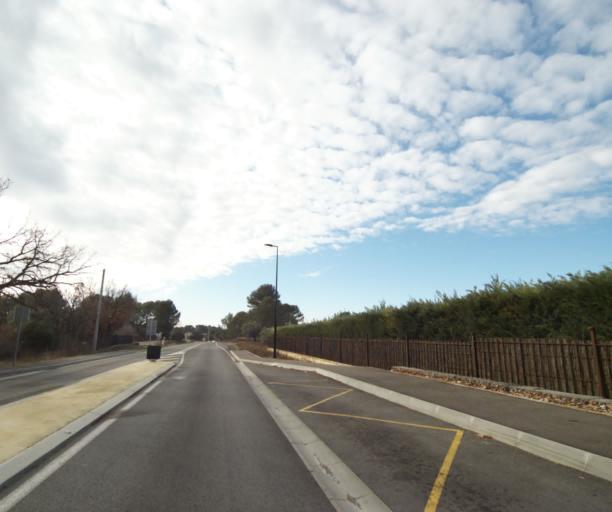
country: FR
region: Provence-Alpes-Cote d'Azur
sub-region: Departement du Var
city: Trans-en-Provence
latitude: 43.4889
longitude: 6.4836
